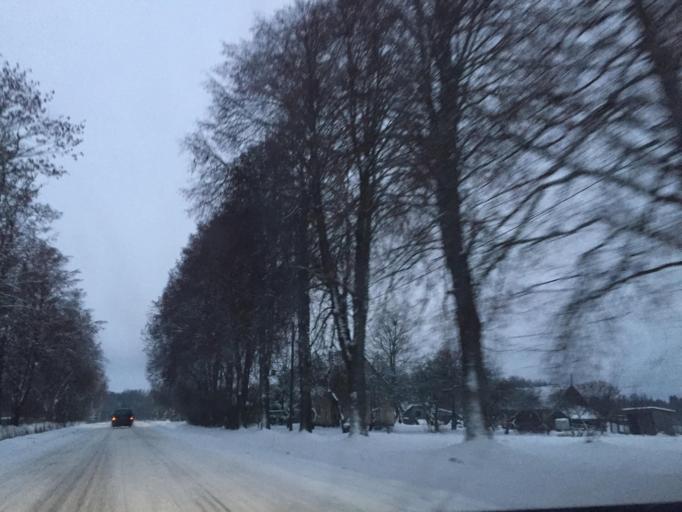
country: LV
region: Raunas
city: Rauna
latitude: 57.4243
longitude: 25.5903
